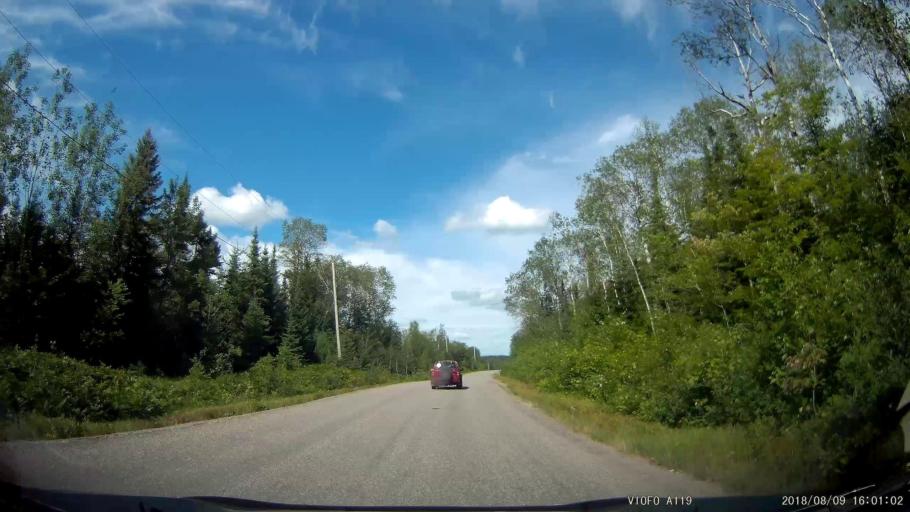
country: CA
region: Ontario
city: Rayside-Balfour
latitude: 46.6097
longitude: -81.4738
